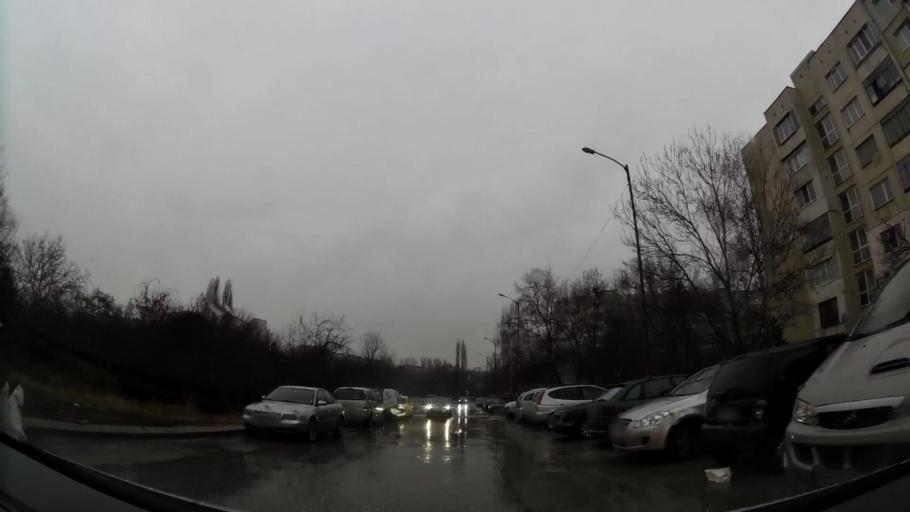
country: BG
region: Sofia-Capital
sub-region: Stolichna Obshtina
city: Sofia
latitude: 42.6556
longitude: 23.3644
